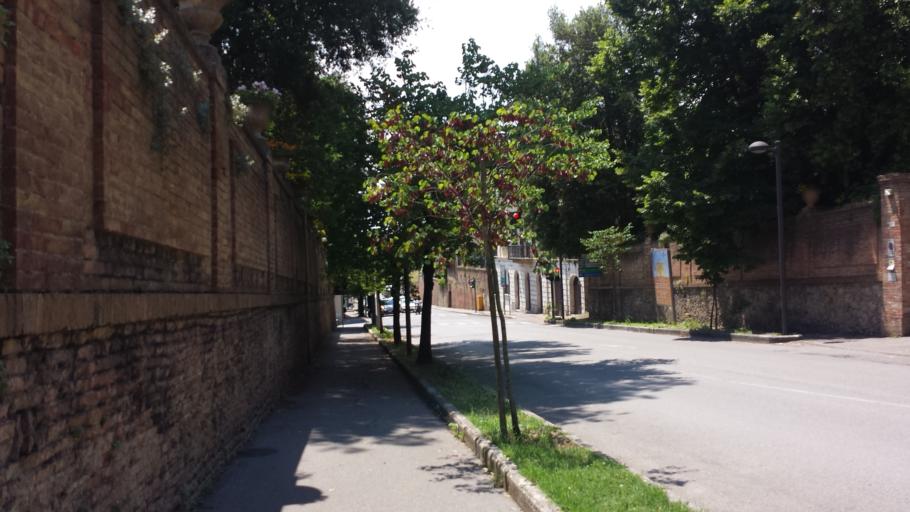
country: IT
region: Tuscany
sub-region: Provincia di Siena
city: Siena
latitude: 43.3123
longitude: 11.3394
